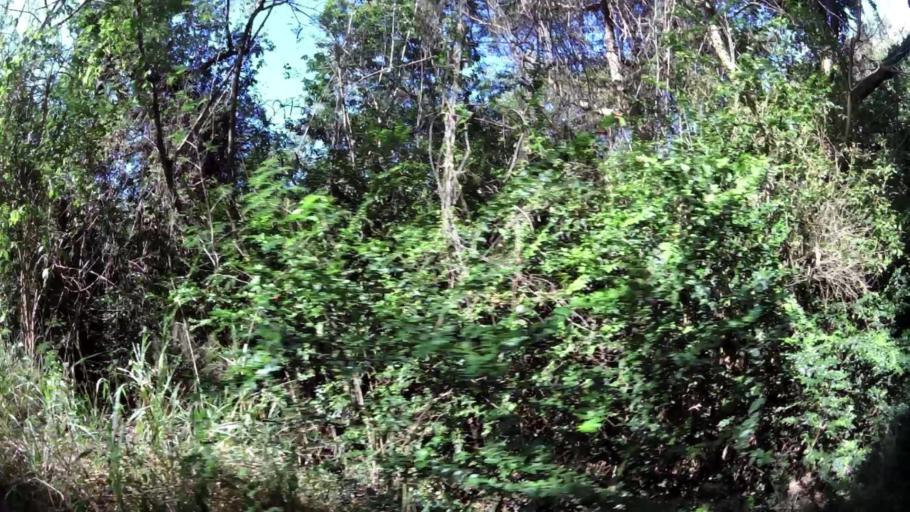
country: VG
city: Road Town
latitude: 18.3926
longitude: -64.7021
